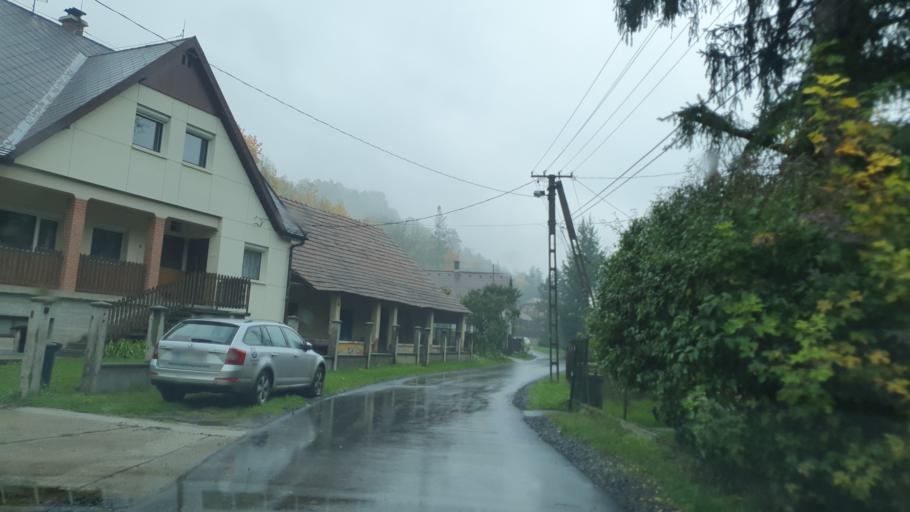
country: HU
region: Komarom-Esztergom
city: Pilismarot
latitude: 47.8052
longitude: 18.9142
